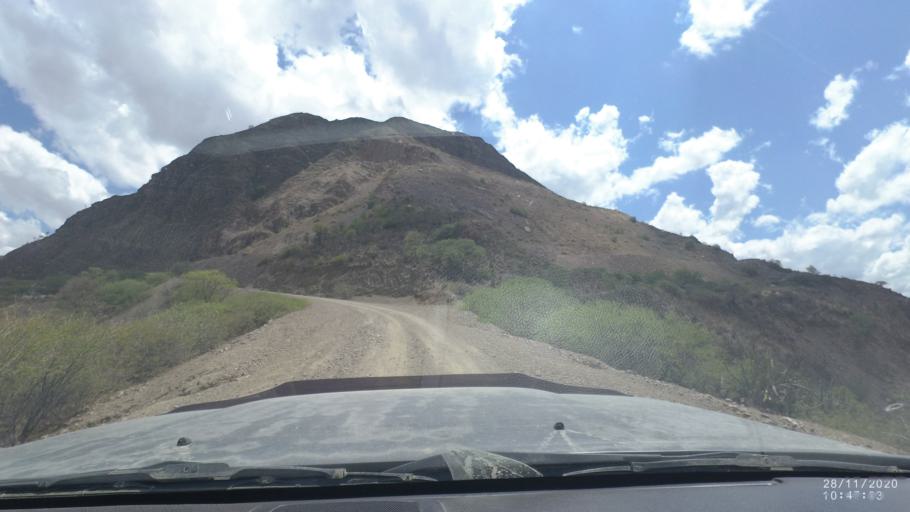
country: BO
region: Cochabamba
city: Capinota
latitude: -17.7865
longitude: -66.1259
